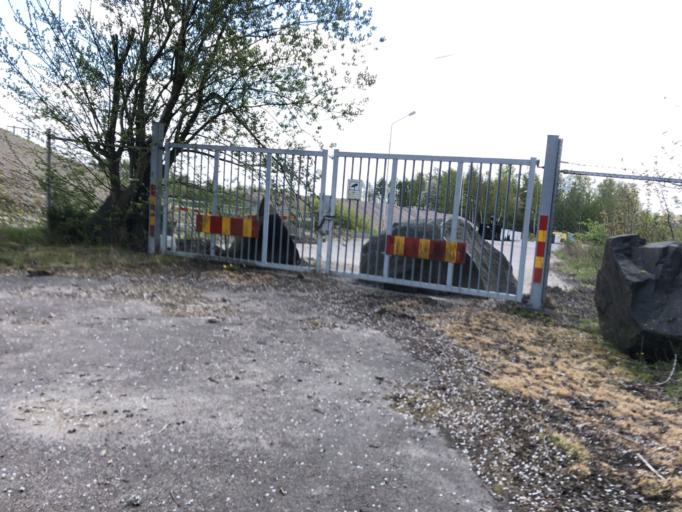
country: SE
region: Skane
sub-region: Lunds Kommun
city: Genarp
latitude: 55.6578
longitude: 13.3771
